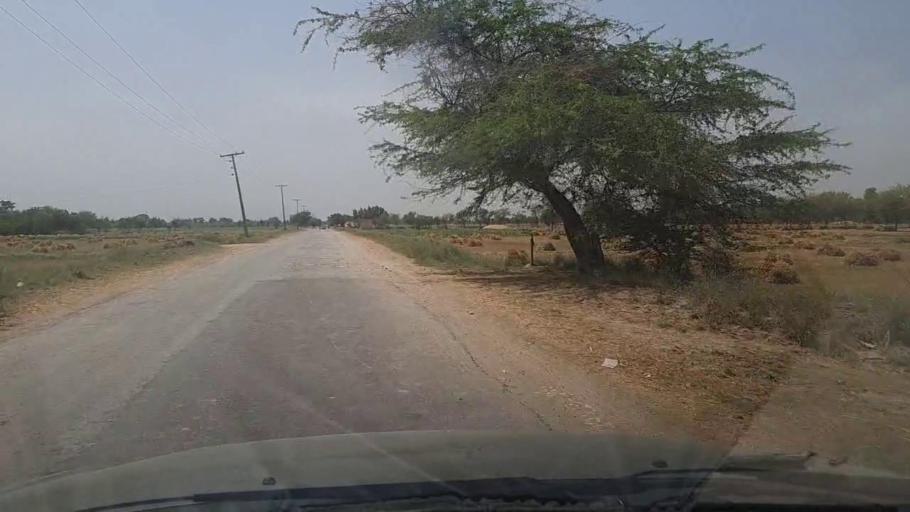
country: PK
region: Sindh
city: Bhiria
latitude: 26.8934
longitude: 68.2468
